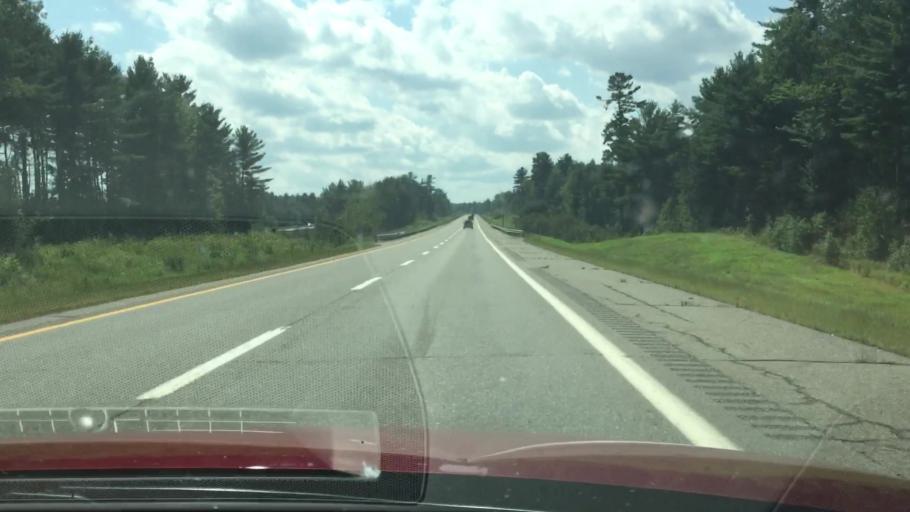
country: US
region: Maine
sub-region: Penobscot County
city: Howland
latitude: 45.3248
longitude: -68.6446
